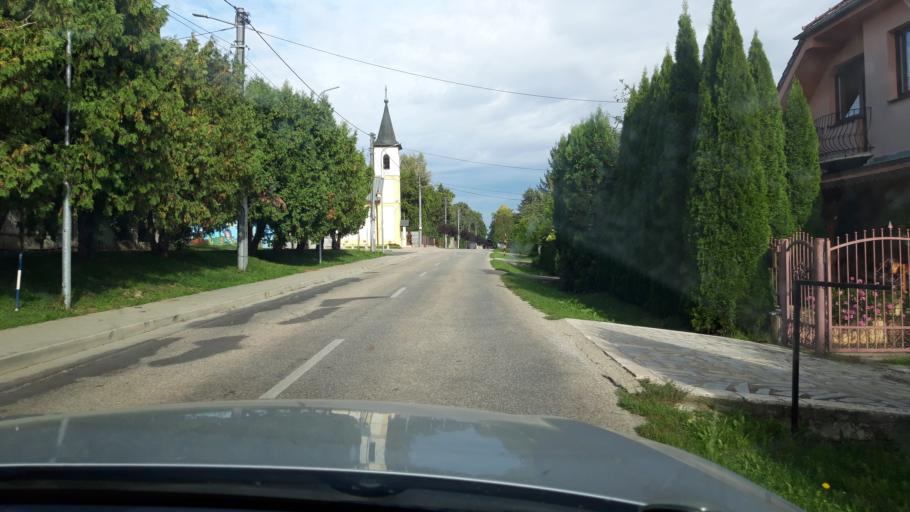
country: SK
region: Nitriansky
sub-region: Okres Nitra
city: Vrable
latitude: 48.1112
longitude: 18.3364
